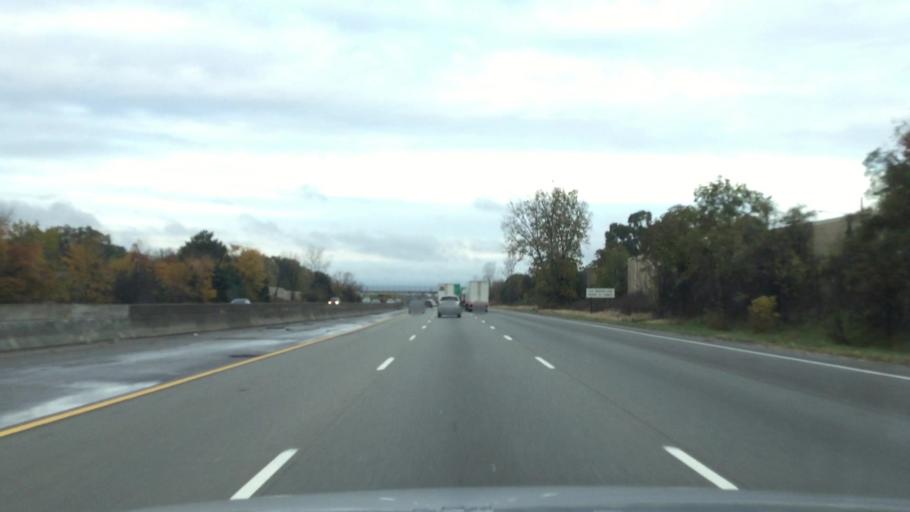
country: US
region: Michigan
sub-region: Washtenaw County
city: Ypsilanti
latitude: 42.2318
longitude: -83.5852
